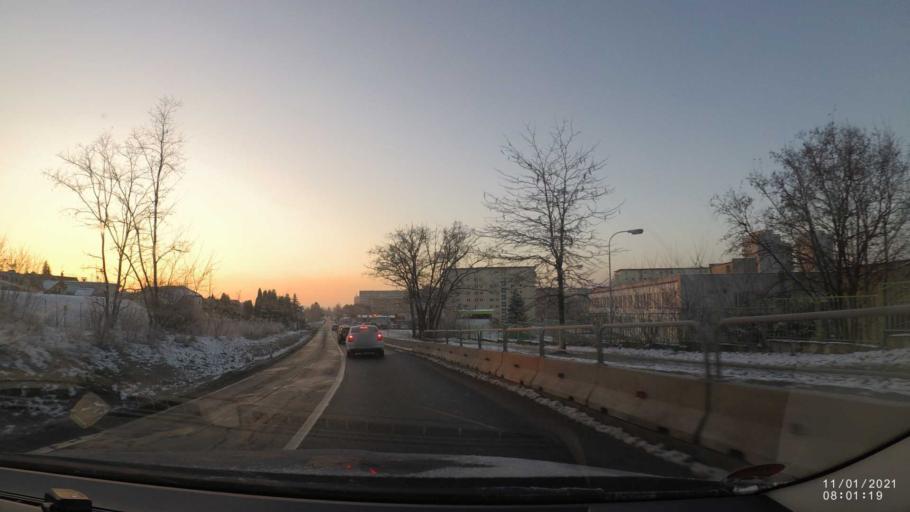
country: CZ
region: South Moravian
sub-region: Mesto Brno
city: Mokra Hora
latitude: 49.2377
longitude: 16.6268
